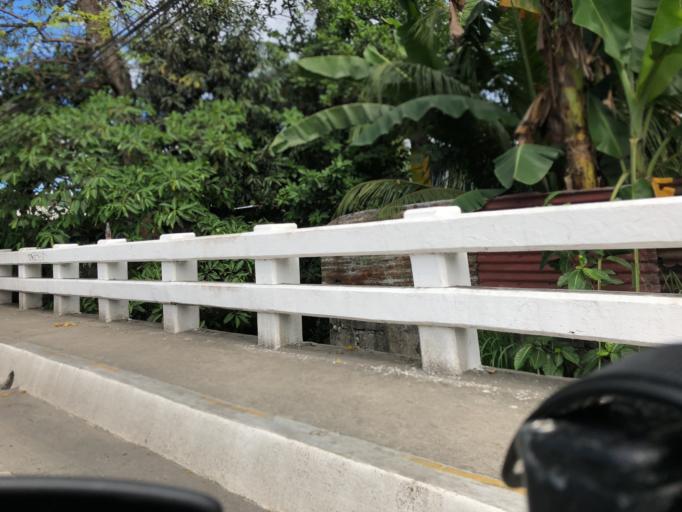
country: PH
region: Calabarzon
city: Bagong Pagasa
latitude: 14.7225
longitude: 121.0612
